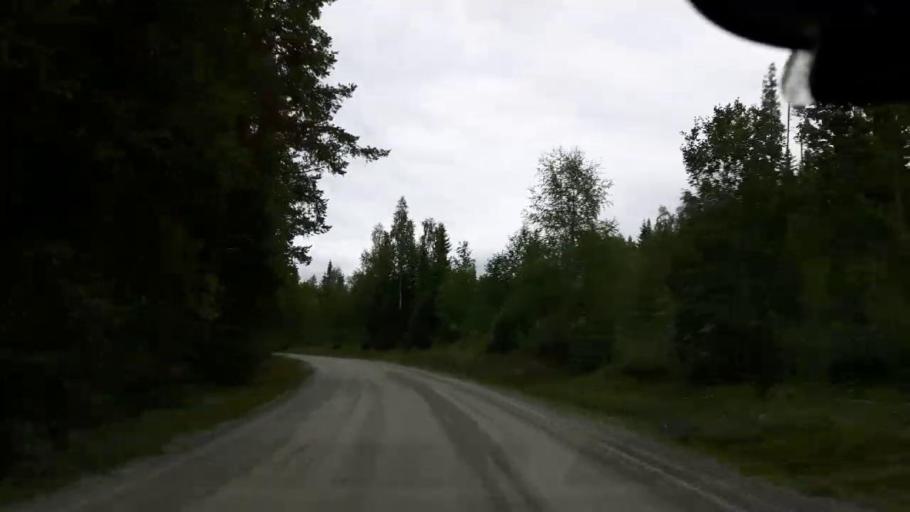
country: SE
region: Jaemtland
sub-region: OEstersunds Kommun
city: Brunflo
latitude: 63.0898
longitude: 15.1632
